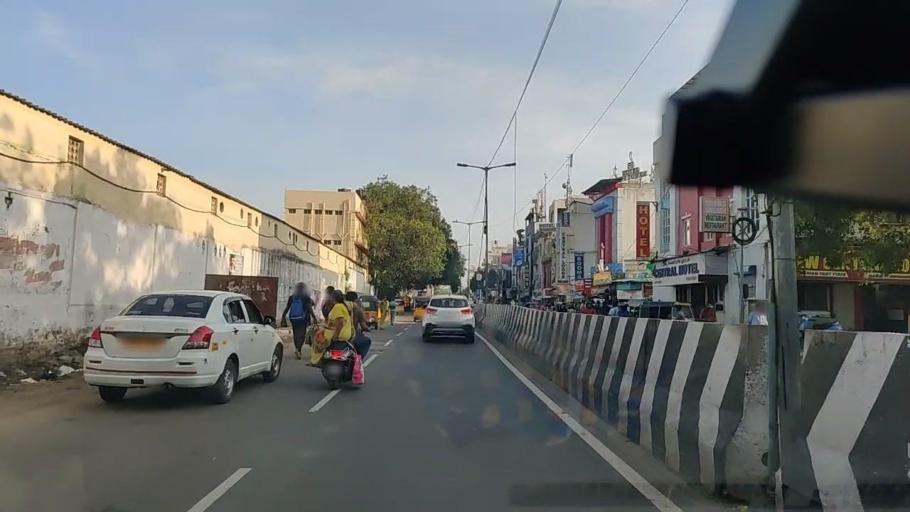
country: IN
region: Tamil Nadu
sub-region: Chennai
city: Chennai
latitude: 13.0832
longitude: 80.2761
